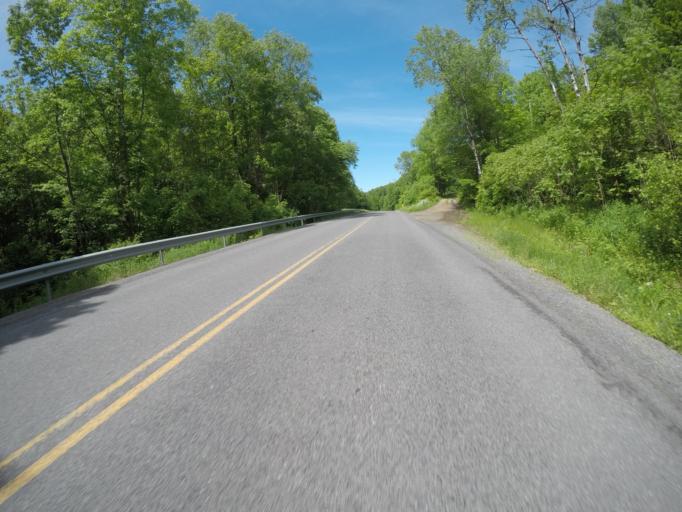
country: US
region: New York
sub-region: Delaware County
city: Delhi
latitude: 42.1085
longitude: -74.8225
